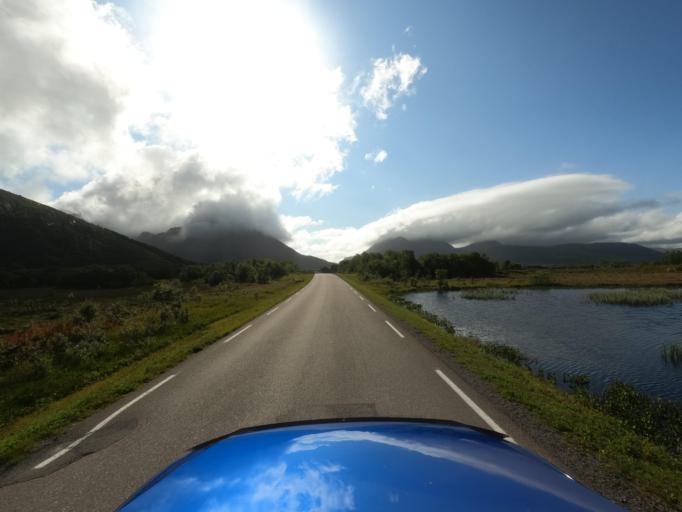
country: NO
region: Nordland
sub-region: Vagan
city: Kabelvag
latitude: 68.3016
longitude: 14.1678
